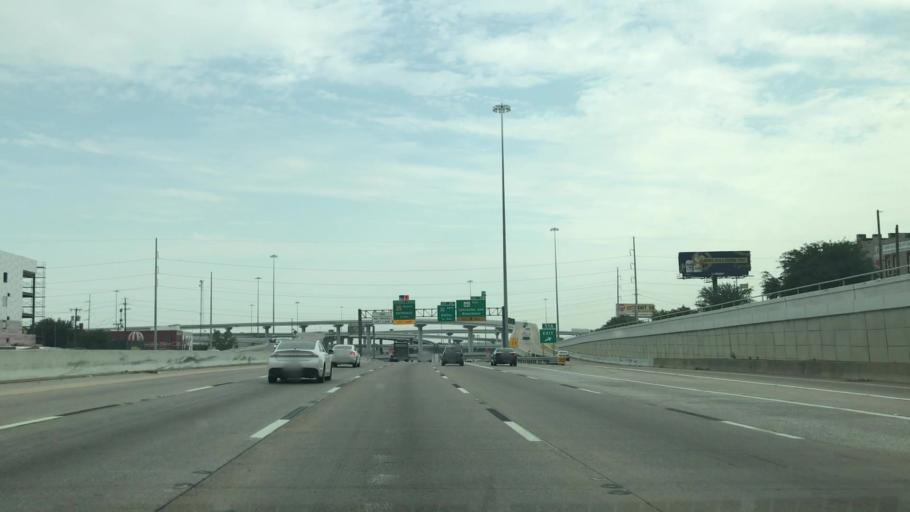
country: US
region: Texas
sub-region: Tarrant County
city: Fort Worth
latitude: 32.7398
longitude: -97.3202
